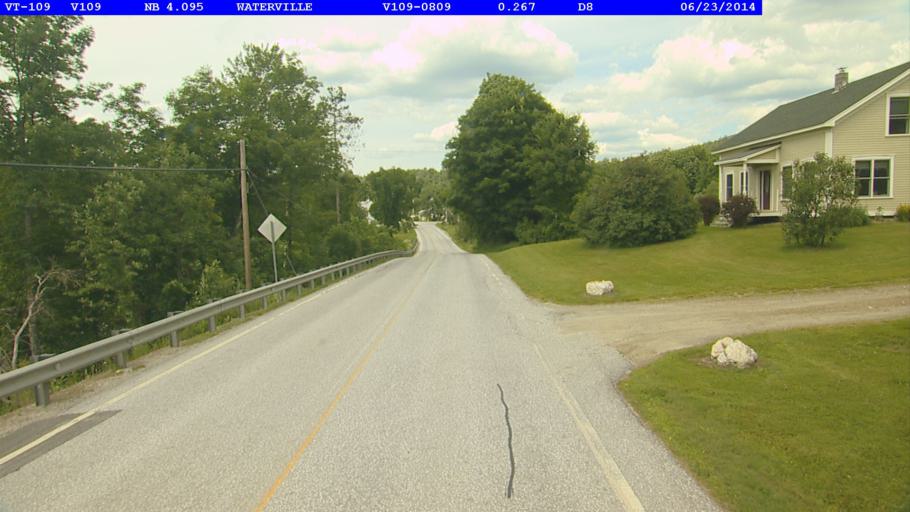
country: US
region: Vermont
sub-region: Lamoille County
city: Johnson
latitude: 44.6865
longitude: -72.7698
